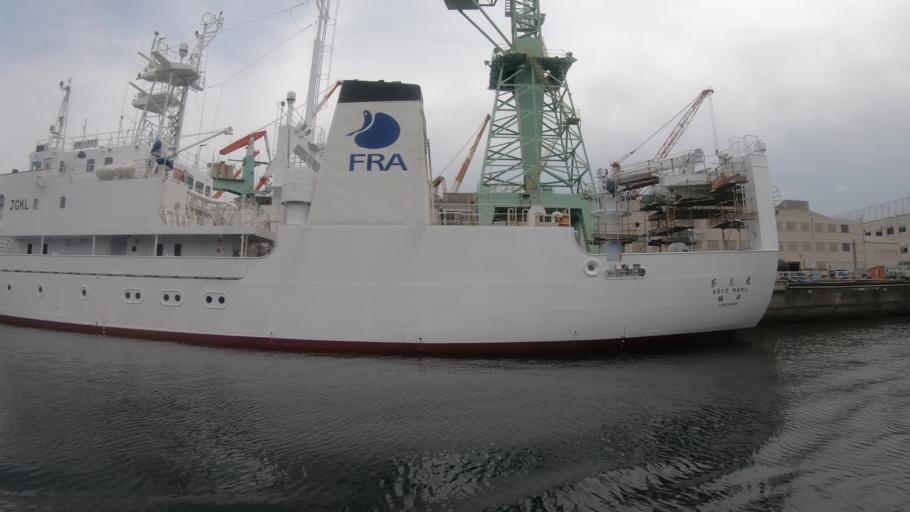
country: JP
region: Kanagawa
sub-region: Kawasaki-shi
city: Kawasaki
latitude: 35.4917
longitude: 139.6888
